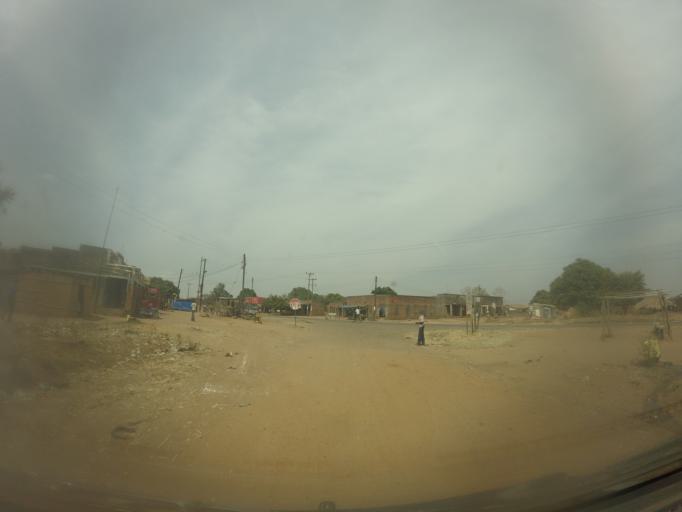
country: UG
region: Northern Region
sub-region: Arua District
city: Arua
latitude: 2.7738
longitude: 31.0368
